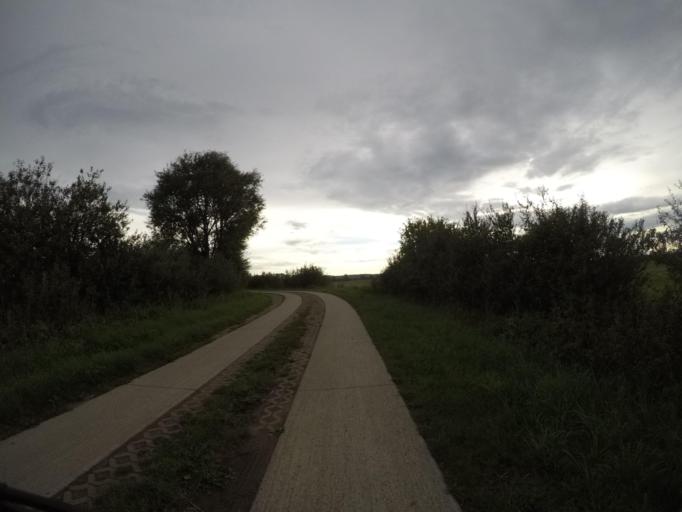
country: DE
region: Lower Saxony
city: Neu Darchau
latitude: 53.2621
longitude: 10.8796
